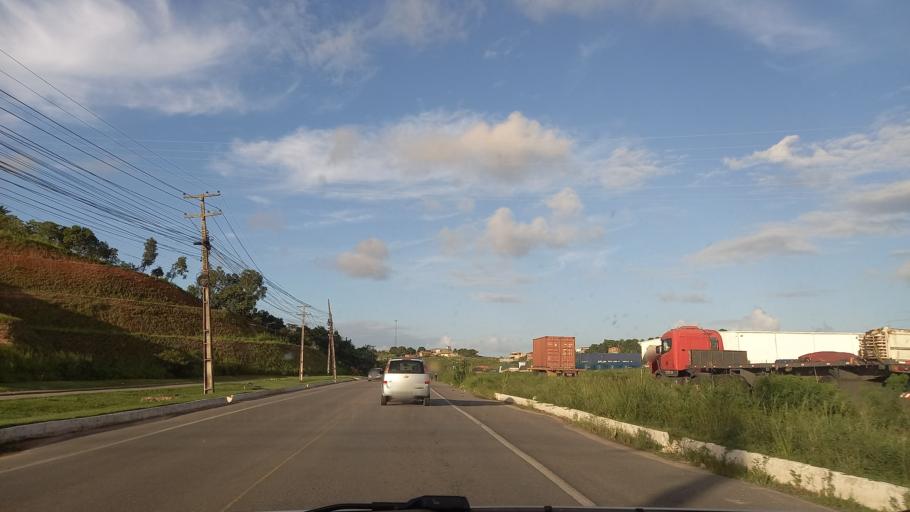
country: BR
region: Pernambuco
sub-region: Cabo De Santo Agostinho
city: Cabo
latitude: -8.2453
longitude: -34.9939
